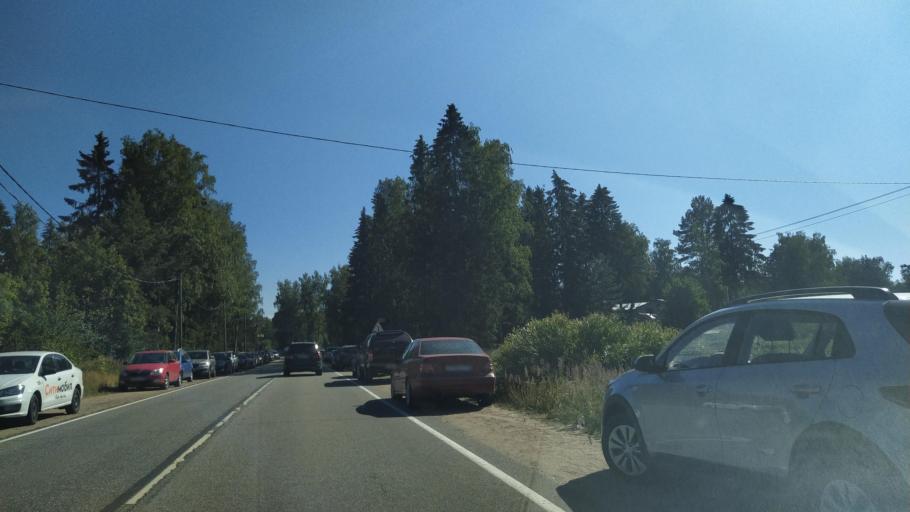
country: RU
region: Leningrad
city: Borisova Griva
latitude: 60.1224
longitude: 31.0744
